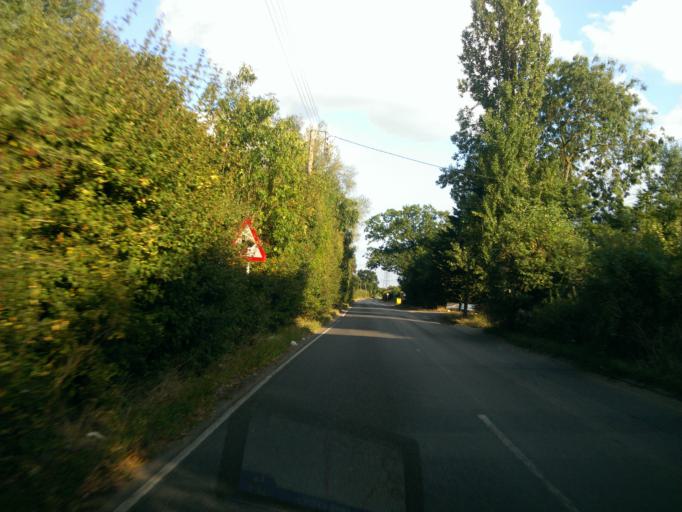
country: GB
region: England
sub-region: Essex
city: Rayne
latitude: 51.8674
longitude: 0.5846
